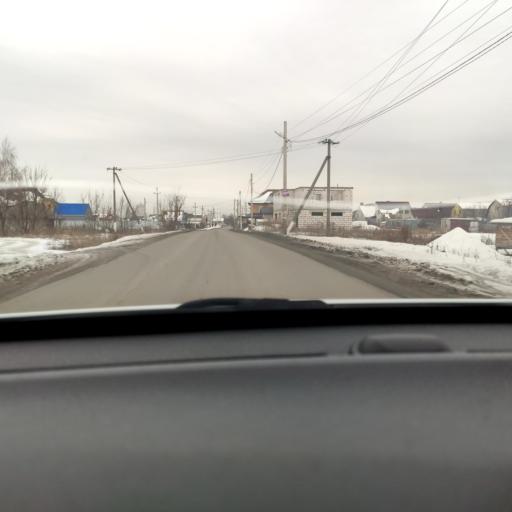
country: RU
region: Voronezj
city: Somovo
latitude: 51.6718
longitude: 39.3396
